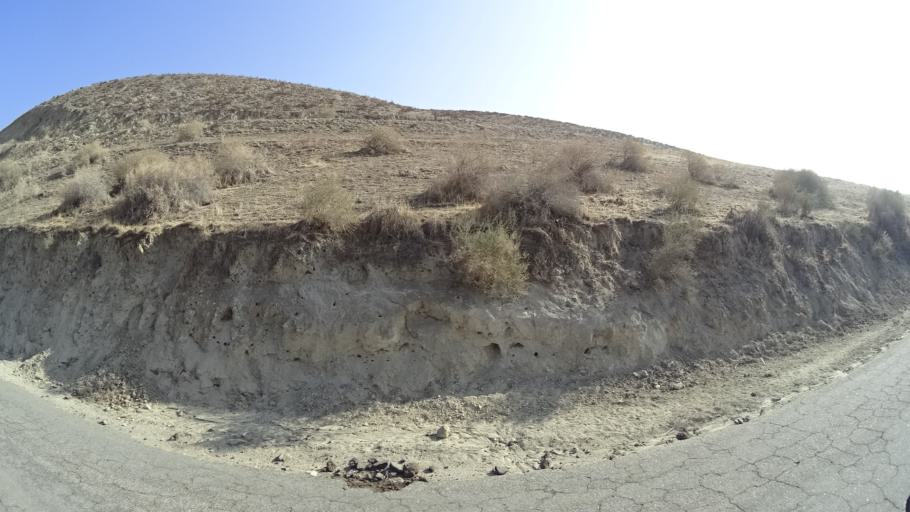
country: US
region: California
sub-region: Kern County
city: Oildale
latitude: 35.4454
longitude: -118.8285
